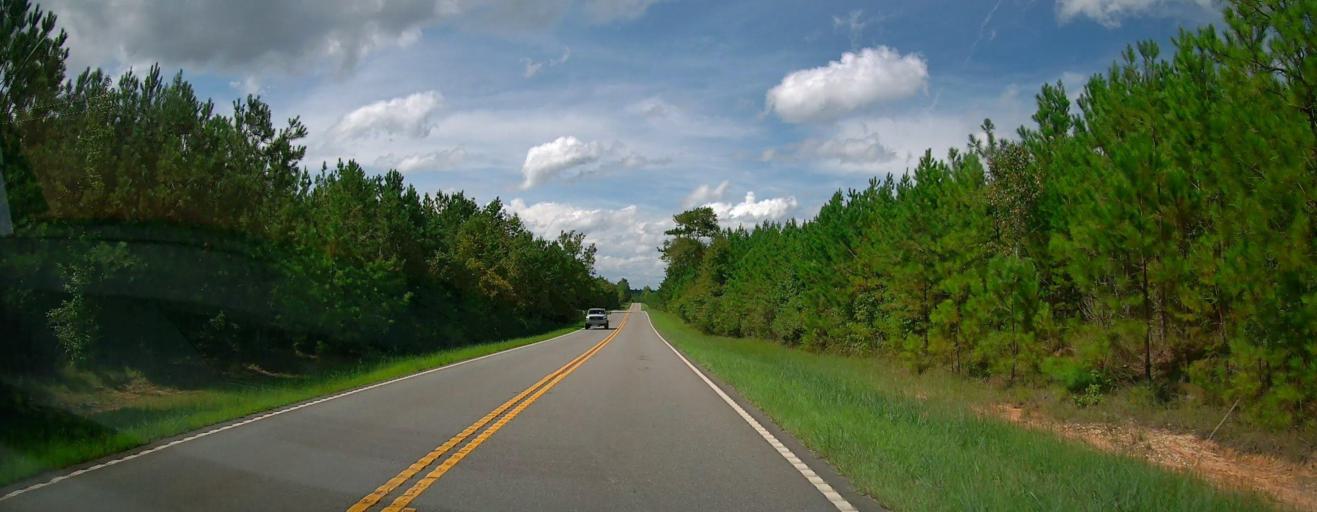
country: US
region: Georgia
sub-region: Talbot County
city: Talbotton
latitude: 32.6572
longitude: -84.5092
